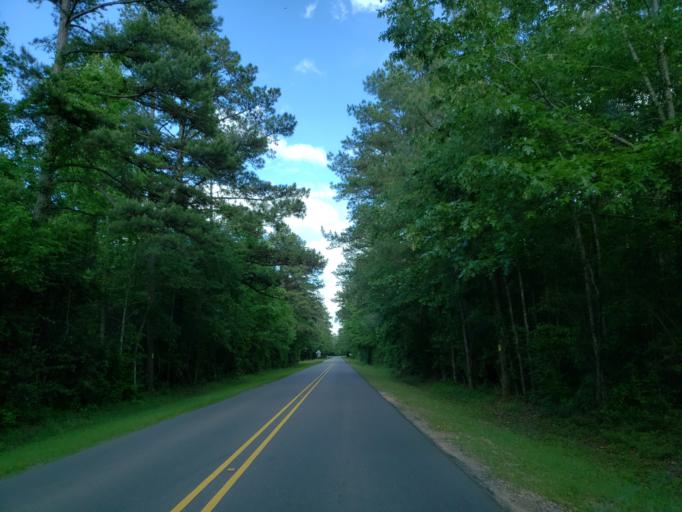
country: US
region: Mississippi
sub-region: Forrest County
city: Petal
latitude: 31.3103
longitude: -89.2336
